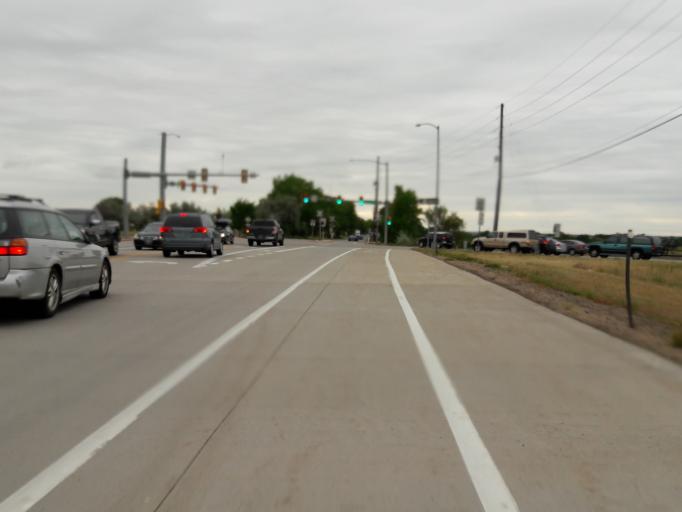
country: US
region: Colorado
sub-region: Boulder County
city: Boulder
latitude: 40.0510
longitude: -105.2339
